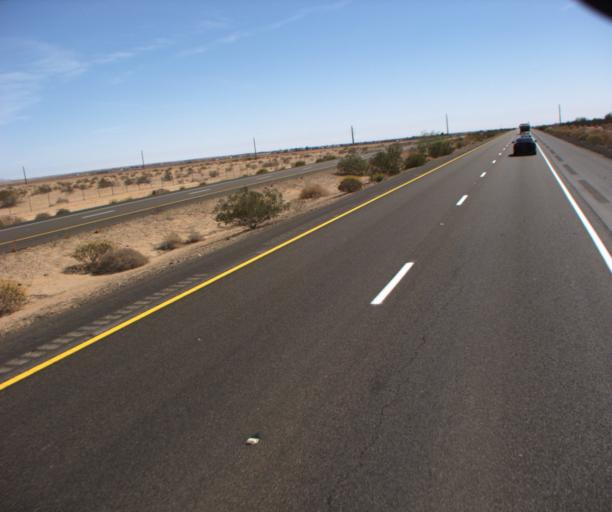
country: US
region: Arizona
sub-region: Yuma County
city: Fortuna Foothills
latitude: 32.6548
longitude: -114.5216
